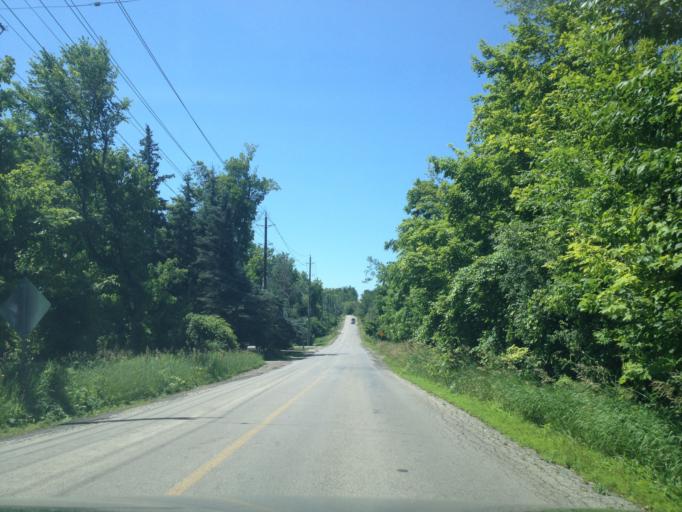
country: CA
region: Ontario
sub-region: Halton
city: Milton
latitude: 43.6649
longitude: -79.9488
